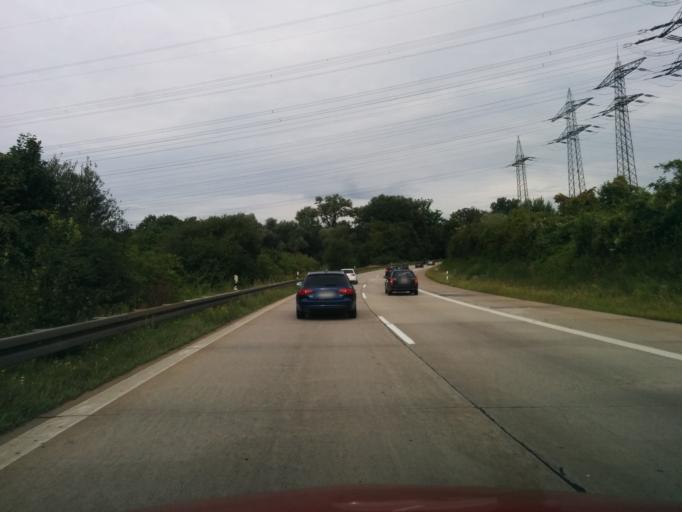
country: DE
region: Baden-Wuerttemberg
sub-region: Karlsruhe Region
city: Ettlingen
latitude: 48.9726
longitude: 8.4416
